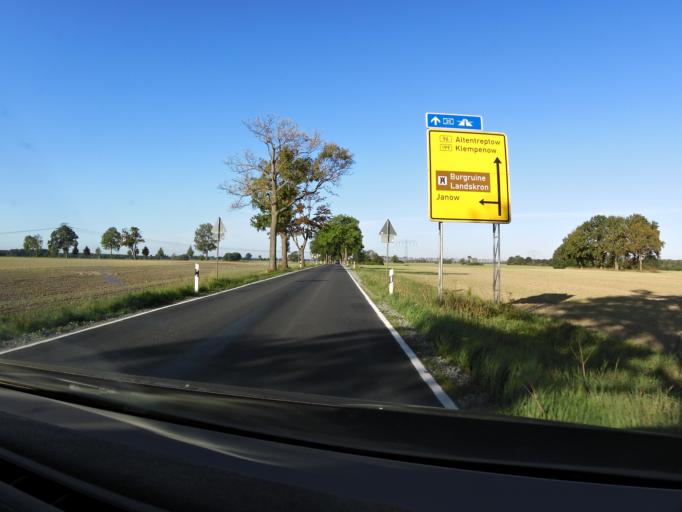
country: DE
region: Mecklenburg-Vorpommern
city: Kessin
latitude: 53.7989
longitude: 13.3881
